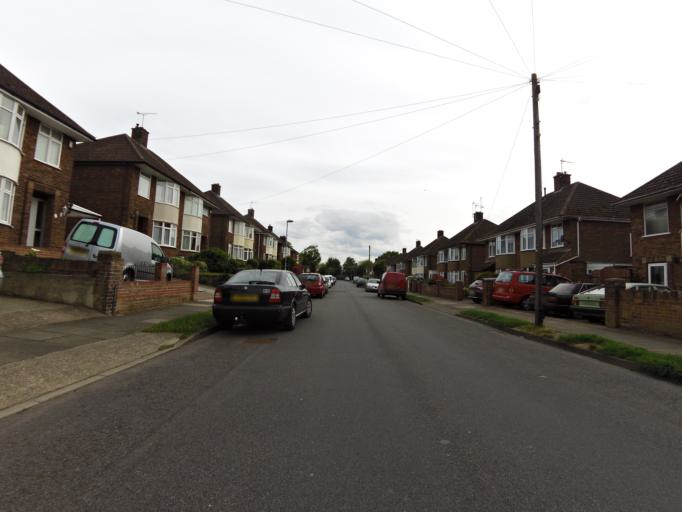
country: GB
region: England
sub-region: Suffolk
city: Ipswich
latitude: 52.0422
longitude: 1.1728
